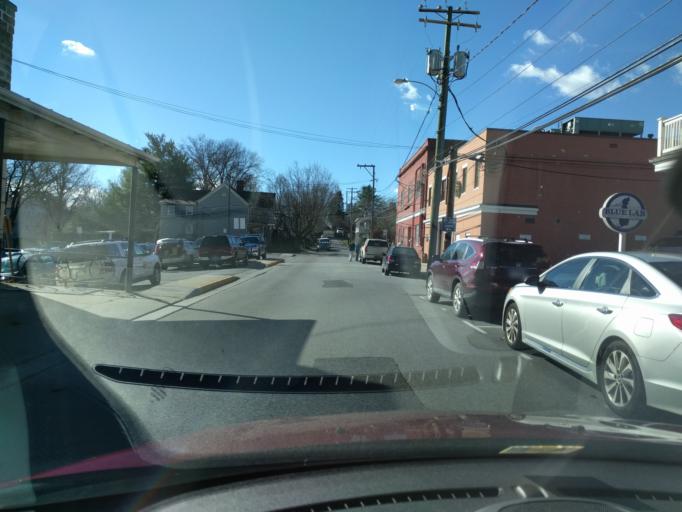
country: US
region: Virginia
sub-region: City of Lexington
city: Lexington
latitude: 37.7828
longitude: -79.4431
